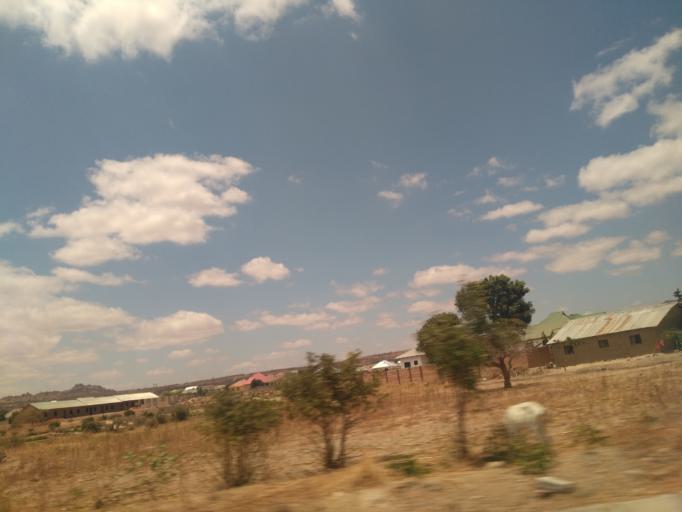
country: TZ
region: Dodoma
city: Kisasa
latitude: -6.1728
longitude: 35.7976
